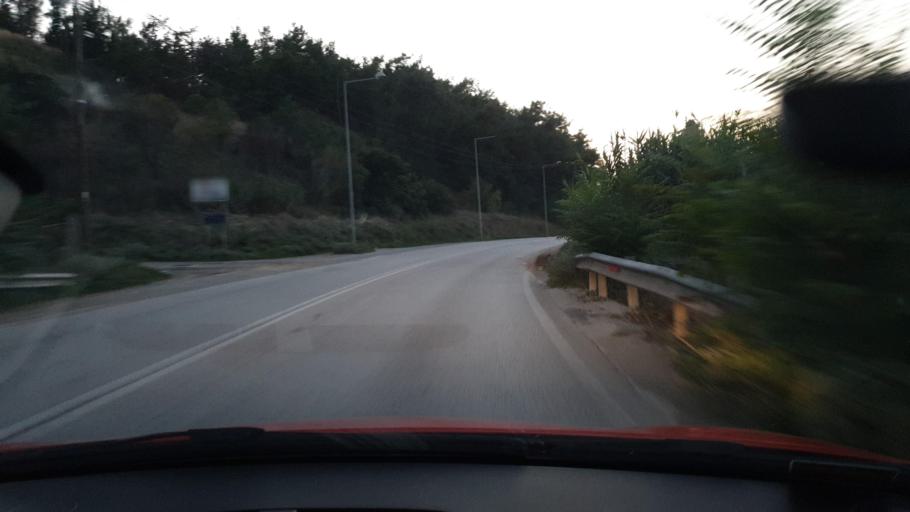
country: GR
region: Central Macedonia
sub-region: Nomos Thessalonikis
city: Agia Triada
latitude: 40.4985
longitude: 22.8805
